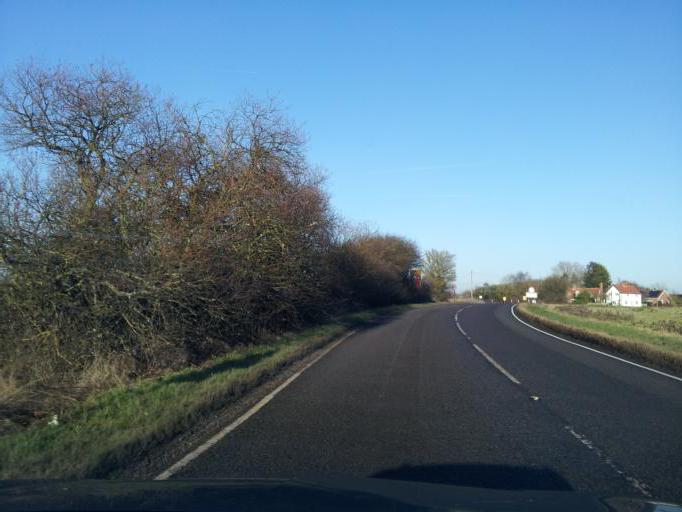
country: GB
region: England
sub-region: Suffolk
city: Lavenham
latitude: 52.1200
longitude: 0.7516
